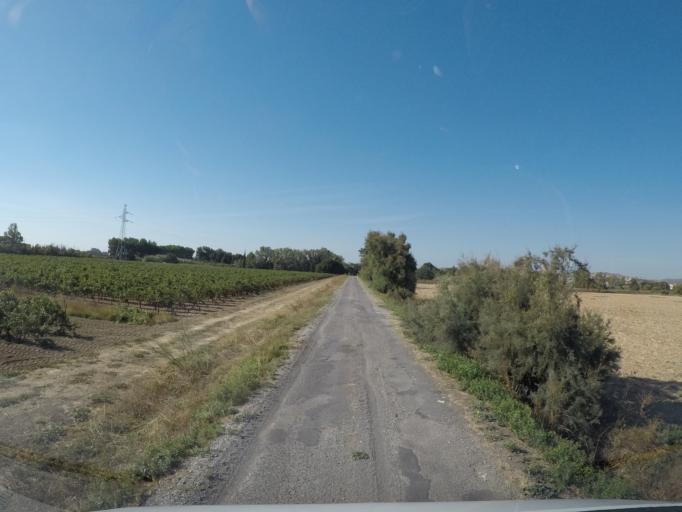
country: FR
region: Languedoc-Roussillon
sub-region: Departement de l'Aude
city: Narbonne
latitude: 43.1727
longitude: 3.0145
